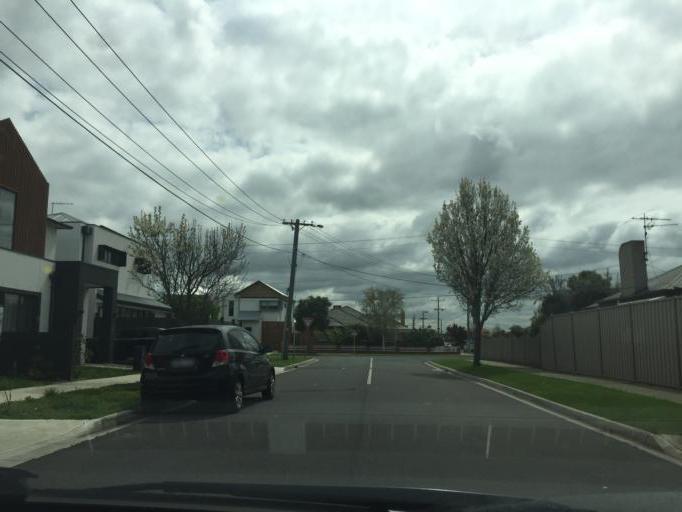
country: AU
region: Victoria
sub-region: Hobsons Bay
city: South Kingsville
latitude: -37.8268
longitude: 144.8723
